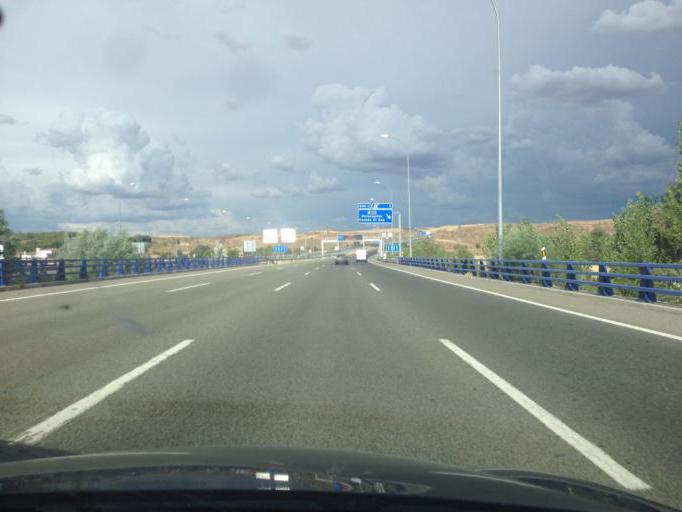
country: ES
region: Madrid
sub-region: Provincia de Madrid
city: Paracuellos de Jarama
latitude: 40.5437
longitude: -3.5571
